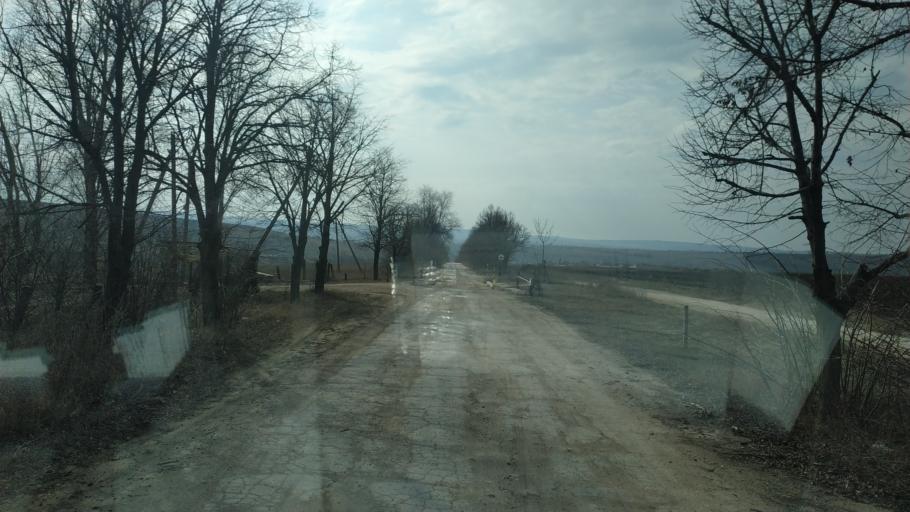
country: MD
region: Anenii Noi
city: Anenii Noi
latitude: 46.9405
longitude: 29.1095
